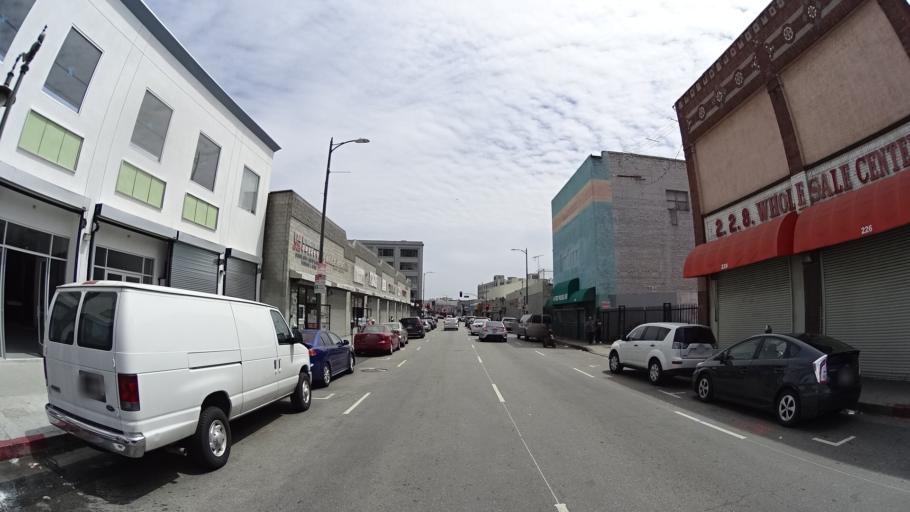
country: US
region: California
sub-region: Los Angeles County
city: Los Angeles
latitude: 34.0466
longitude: -118.2455
